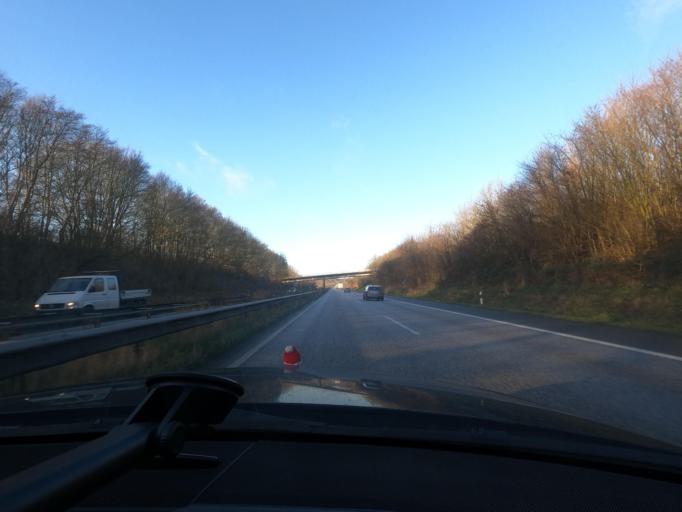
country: DE
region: Schleswig-Holstein
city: Dannewerk
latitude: 54.4969
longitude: 9.5164
